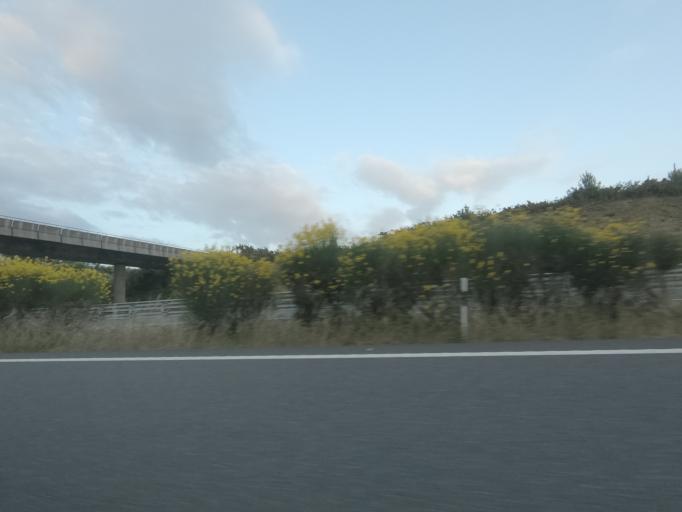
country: ES
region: Galicia
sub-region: Provincia de Ourense
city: Melon
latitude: 42.2240
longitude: -8.2437
